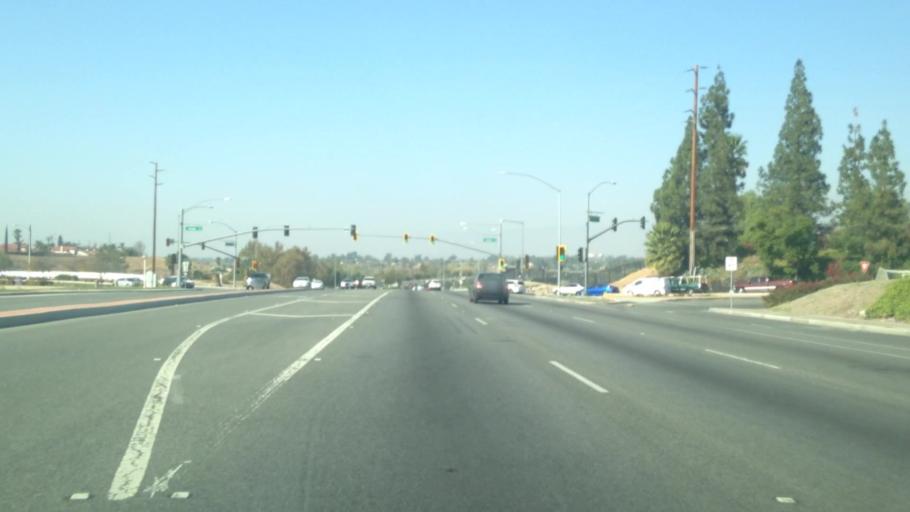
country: US
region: California
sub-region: Riverside County
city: Pedley
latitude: 33.9580
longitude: -117.4604
